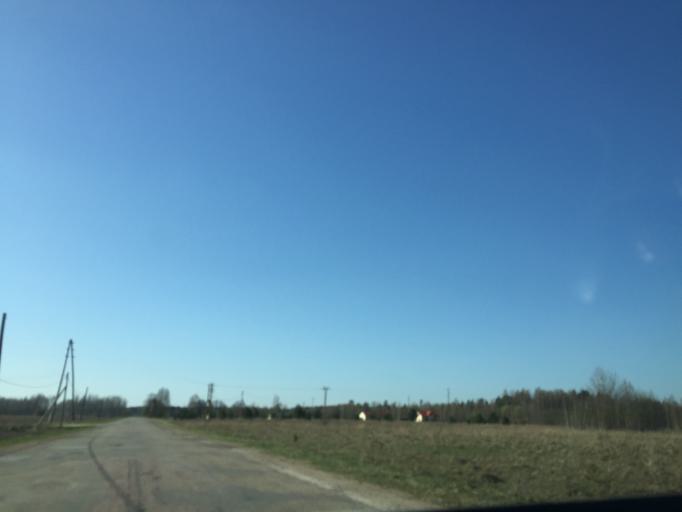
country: LV
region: Ropazu
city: Ropazi
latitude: 56.9587
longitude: 24.6941
